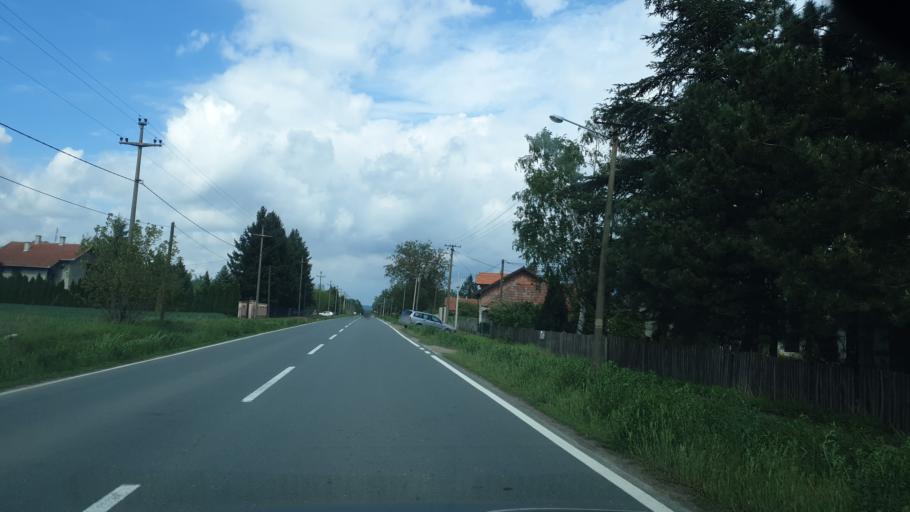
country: RS
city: Stubline
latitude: 44.5442
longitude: 20.1314
